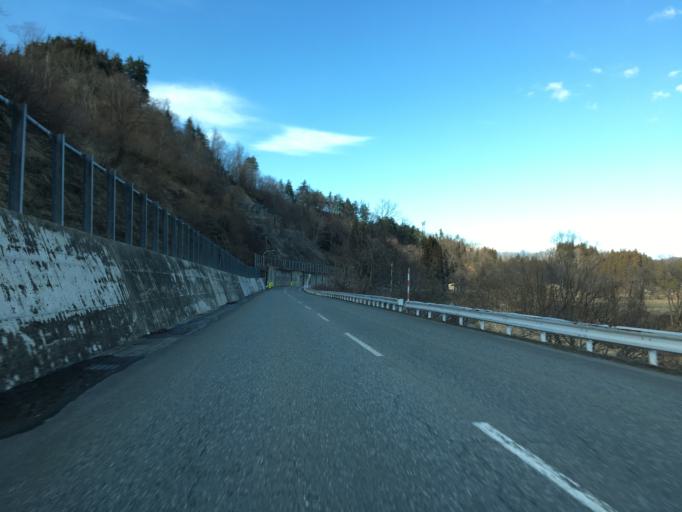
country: JP
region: Yamagata
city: Nagai
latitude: 37.9807
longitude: 139.9444
